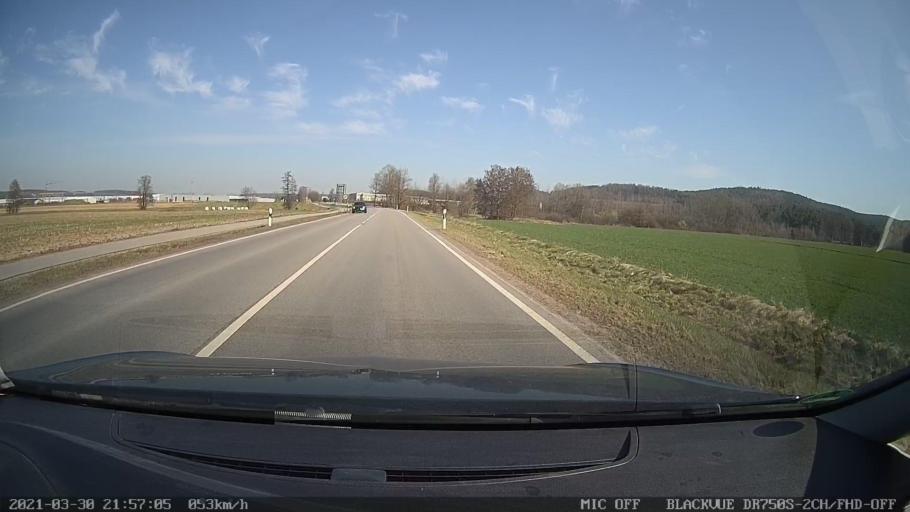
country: DE
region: Bavaria
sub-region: Upper Palatinate
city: Regenstauf
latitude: 49.1006
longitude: 12.1249
